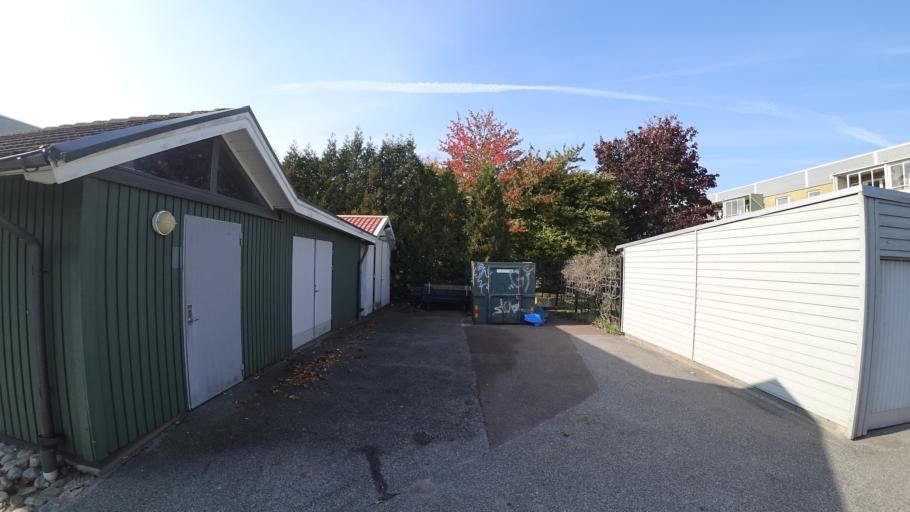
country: SE
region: Skane
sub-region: Staffanstorps Kommun
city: Staffanstorp
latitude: 55.6454
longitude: 13.2005
